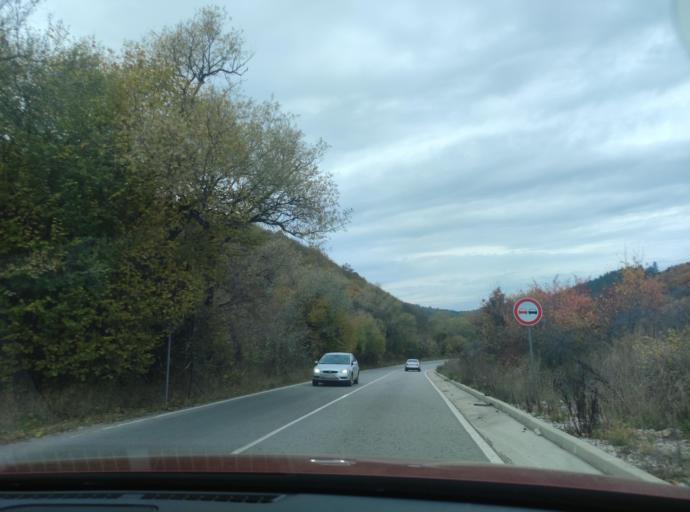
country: BG
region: Sofiya
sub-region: Obshtina Godech
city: Godech
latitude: 42.9661
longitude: 23.1508
